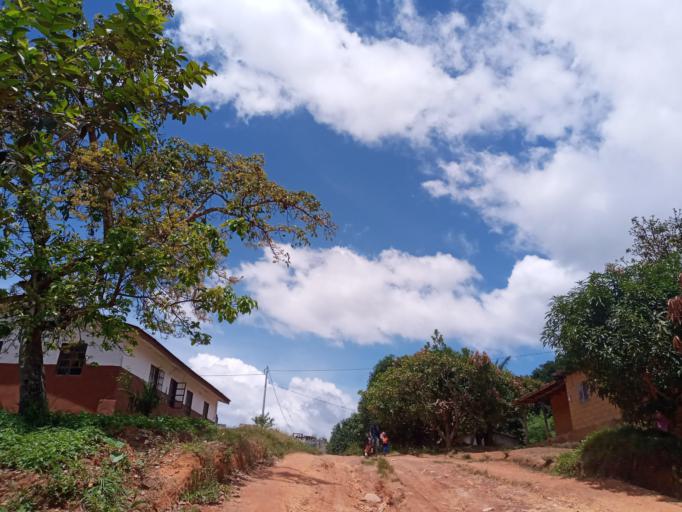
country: SL
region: Eastern Province
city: Tombu
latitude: 8.6274
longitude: -10.8233
